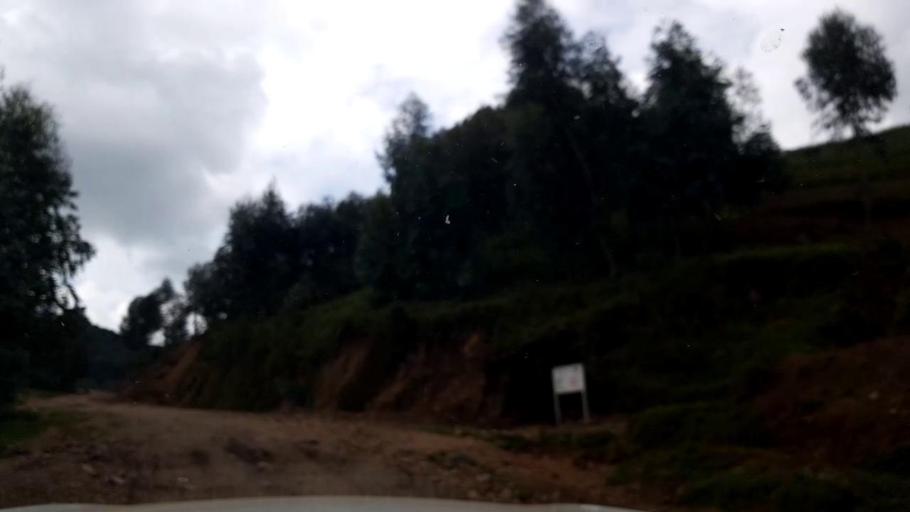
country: RW
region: Western Province
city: Kibuye
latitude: -1.9015
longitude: 29.4546
